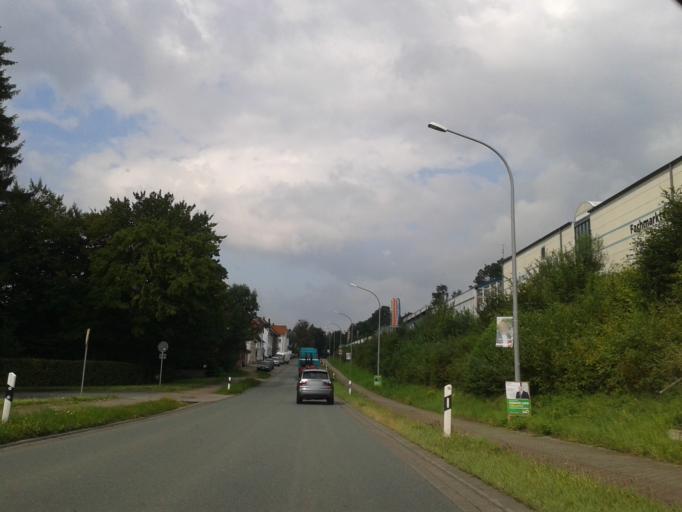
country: DE
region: North Rhine-Westphalia
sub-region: Regierungsbezirk Detmold
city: Blomberg
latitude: 51.9381
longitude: 9.0962
